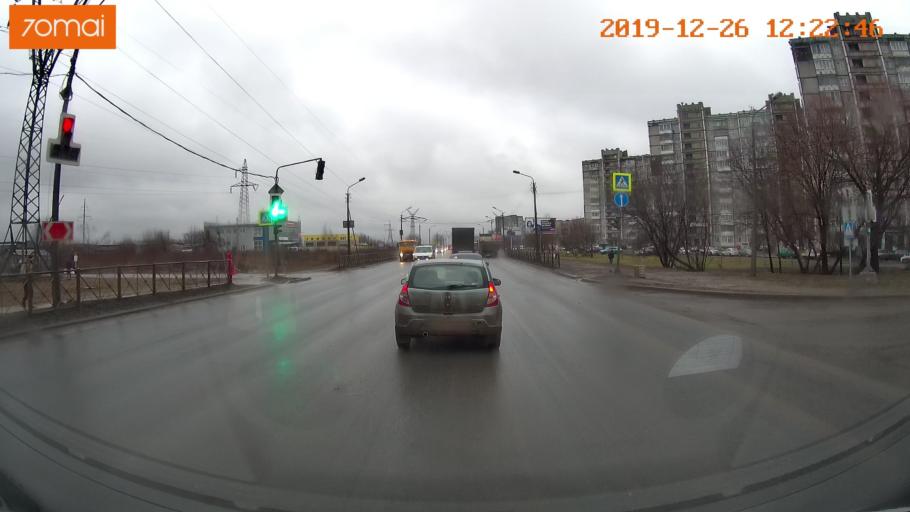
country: RU
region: Vologda
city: Tonshalovo
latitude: 59.1503
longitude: 37.9490
